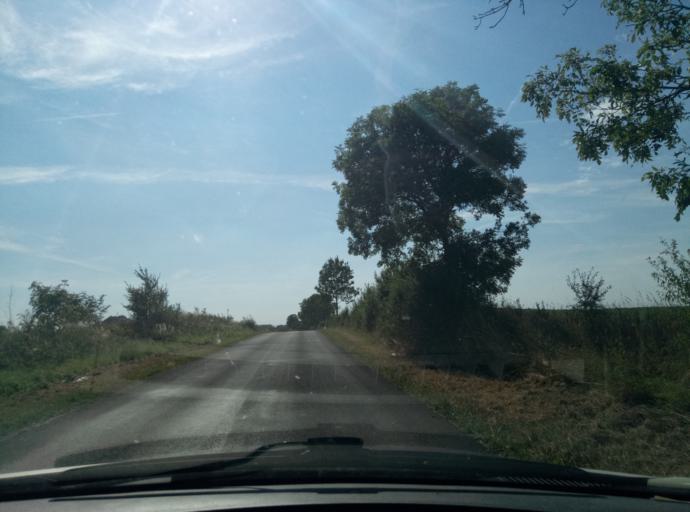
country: PL
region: Kujawsko-Pomorskie
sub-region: Powiat brodnicki
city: Jablonowo Pomorskie
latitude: 53.3936
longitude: 19.1861
